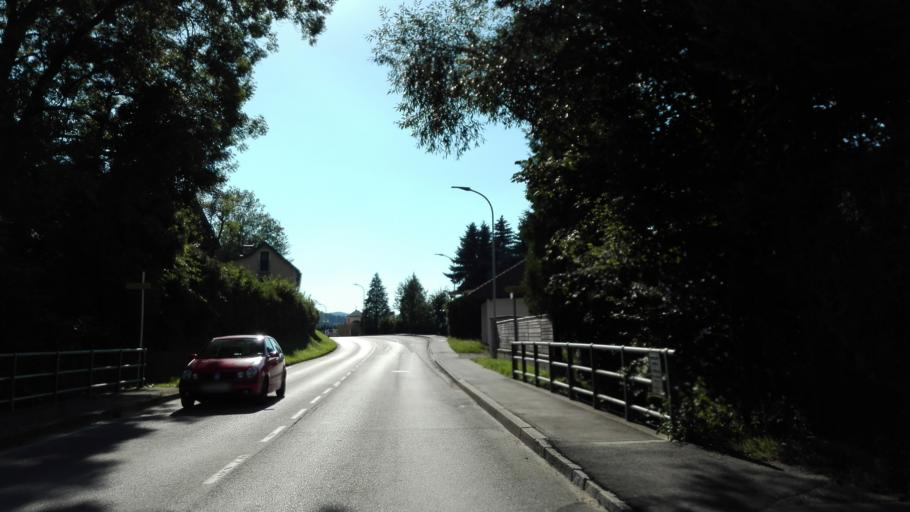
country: AT
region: Lower Austria
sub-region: Politischer Bezirk Sankt Polten
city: Altlengbach
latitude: 48.1532
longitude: 15.9416
